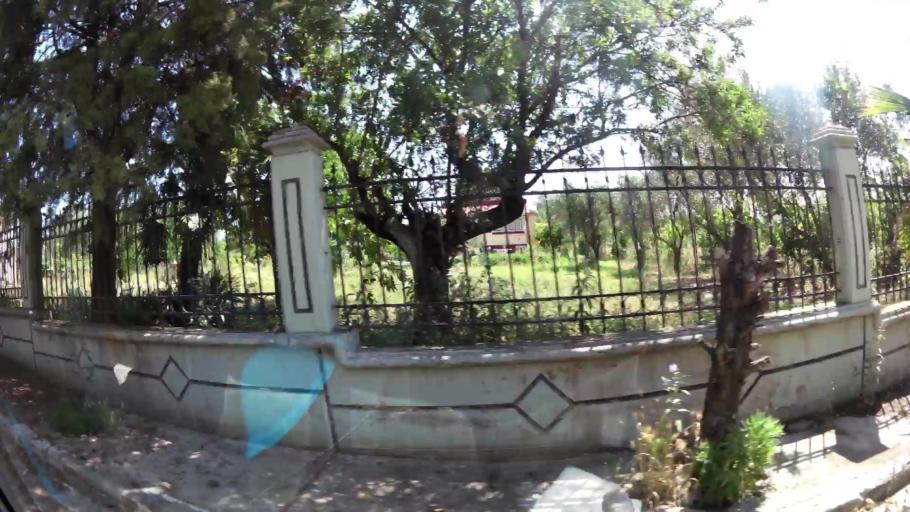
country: GR
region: Central Macedonia
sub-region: Nomos Thessalonikis
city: Agia Triada
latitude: 40.4982
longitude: 22.8366
